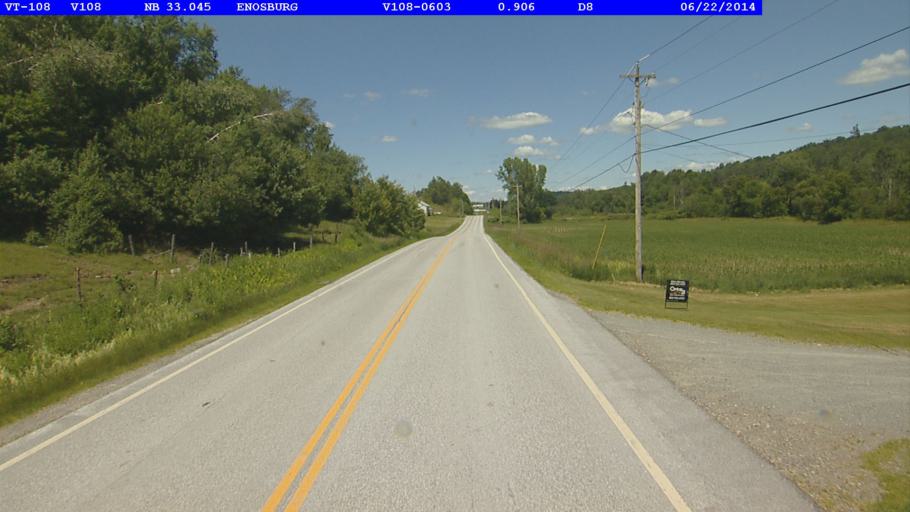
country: US
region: Vermont
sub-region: Franklin County
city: Enosburg Falls
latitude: 44.8511
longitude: -72.8047
